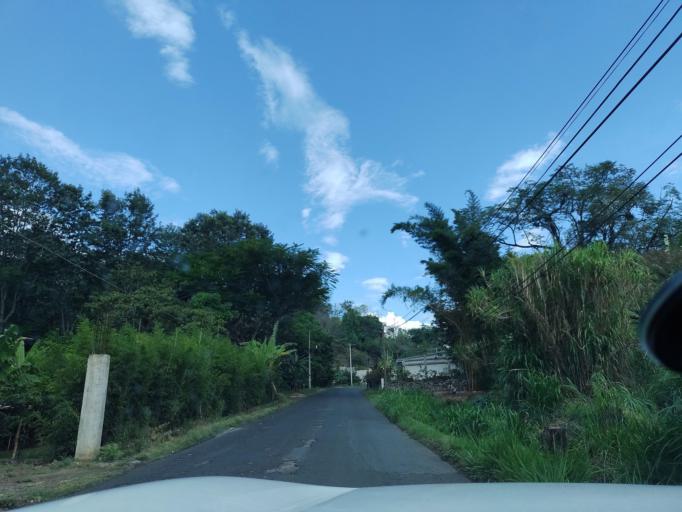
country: MX
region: Veracruz
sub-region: Coatepec
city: Las Lomas
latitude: 19.4814
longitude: -96.9269
